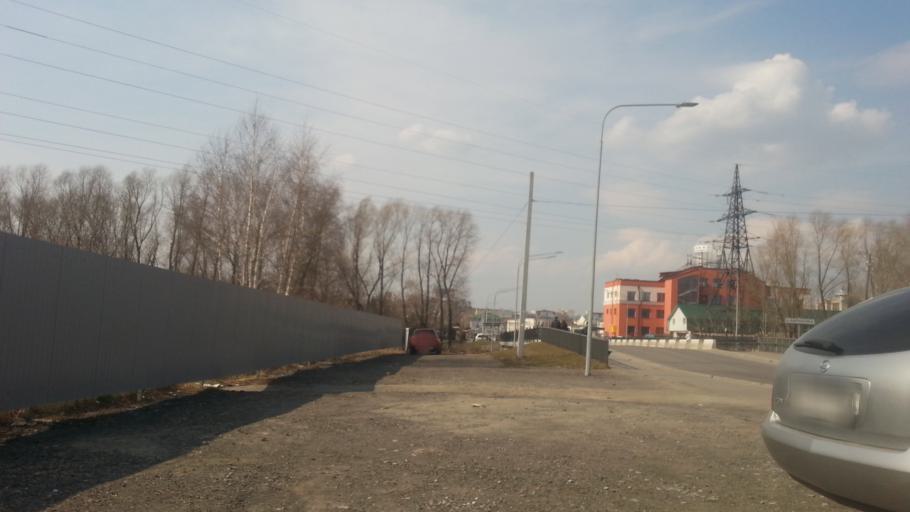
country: RU
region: Altai Krai
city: Zaton
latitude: 53.3271
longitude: 83.7925
